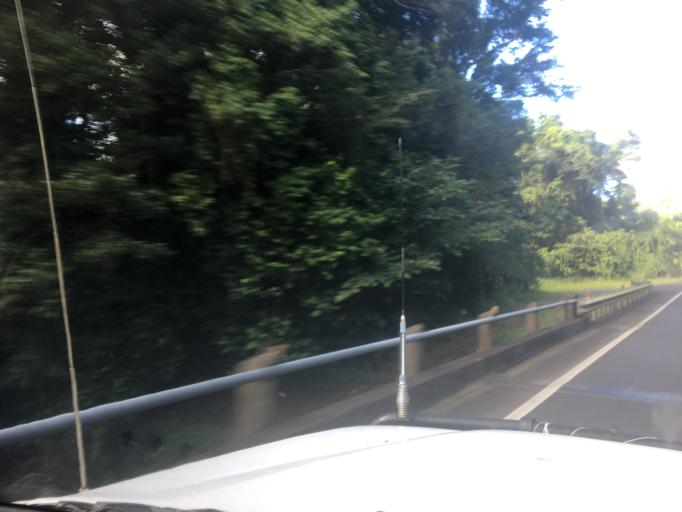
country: AU
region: Queensland
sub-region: Cassowary Coast
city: Innisfail
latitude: -17.2598
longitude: 145.9216
